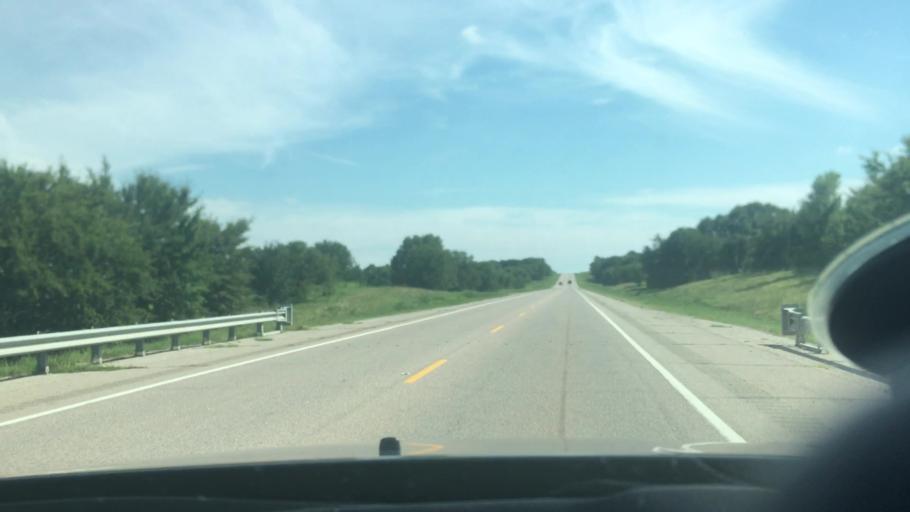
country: US
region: Oklahoma
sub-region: Seminole County
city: Maud
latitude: 35.1267
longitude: -96.6790
